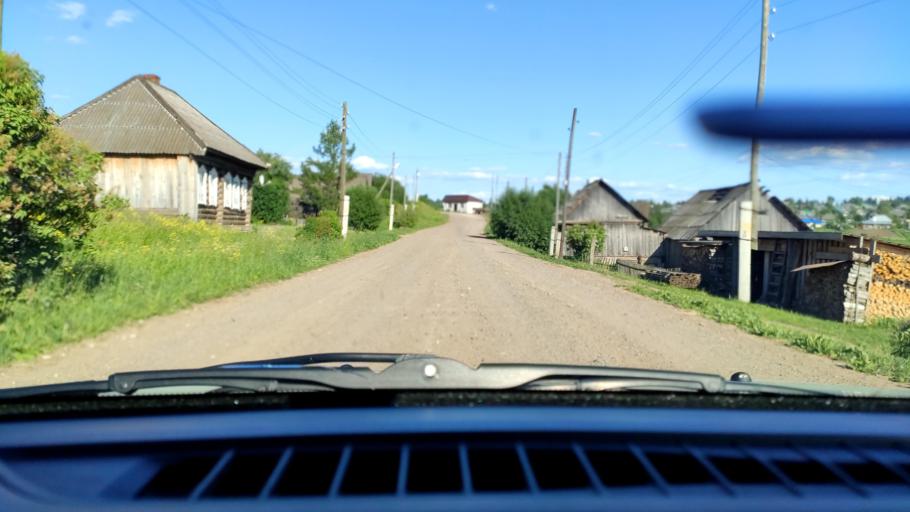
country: RU
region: Perm
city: Uinskoye
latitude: 57.1176
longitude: 56.5101
